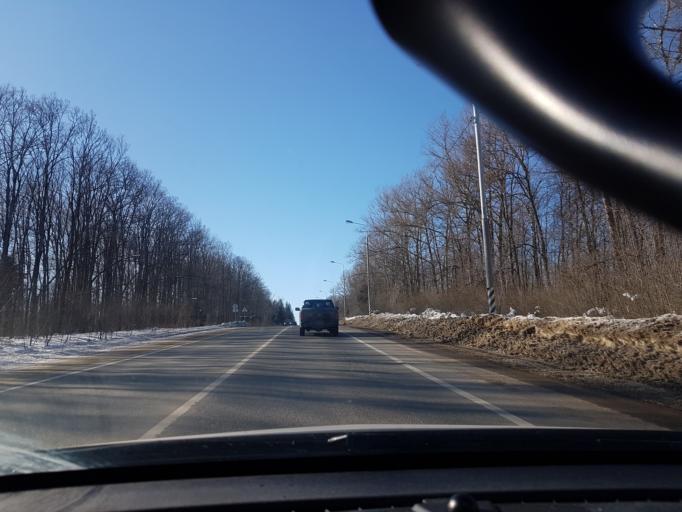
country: RU
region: Moskovskaya
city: Kostrovo
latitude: 55.9125
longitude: 36.7529
